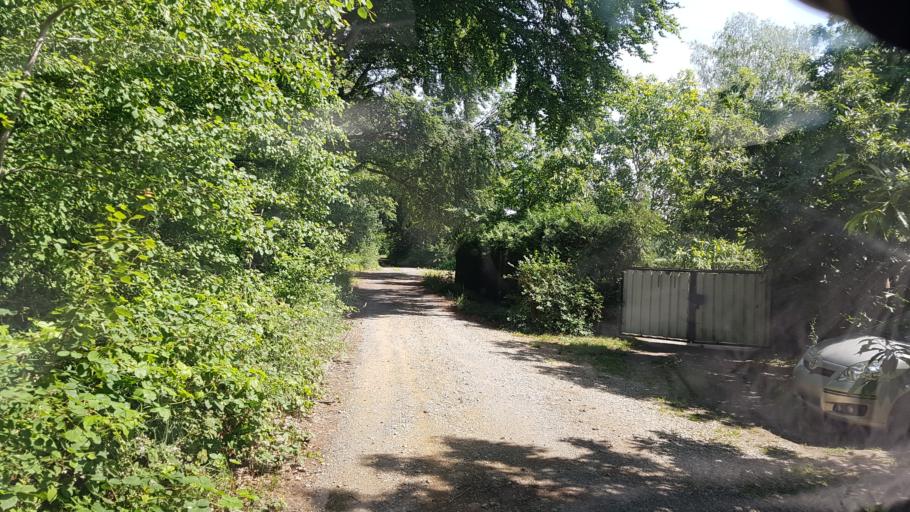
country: DE
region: Brandenburg
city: Doberlug-Kirchhain
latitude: 51.6145
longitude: 13.5420
